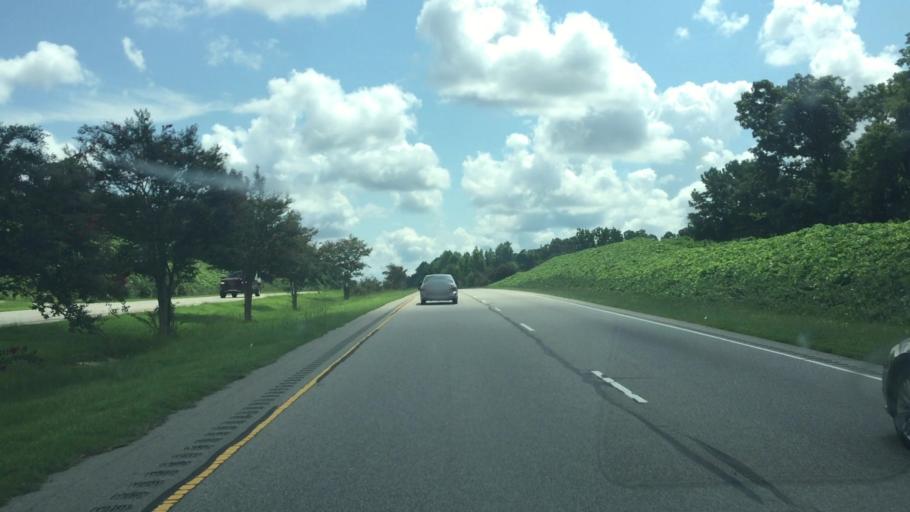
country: US
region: North Carolina
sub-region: Anson County
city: Wadesboro
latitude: 34.9621
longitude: -79.9803
